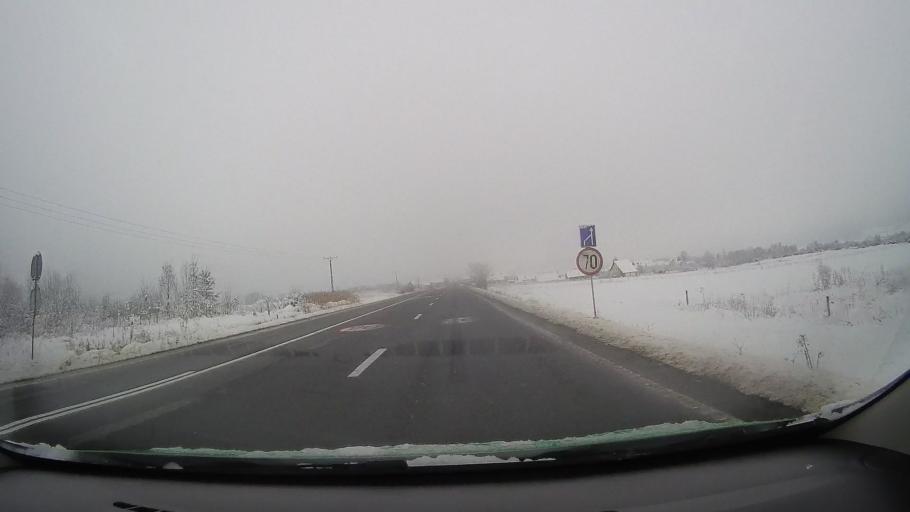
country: RO
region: Sibiu
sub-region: Oras Saliste
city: Saliste
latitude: 45.7875
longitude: 23.9303
